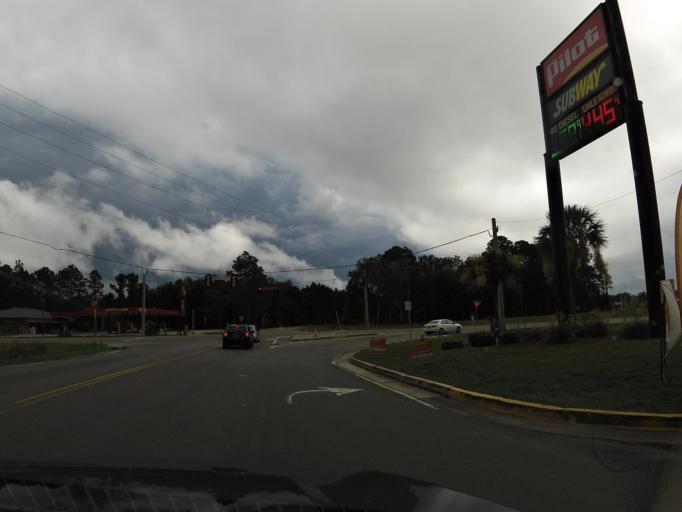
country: US
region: Georgia
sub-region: Camden County
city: Kingsland
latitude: 30.7605
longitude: -81.6482
